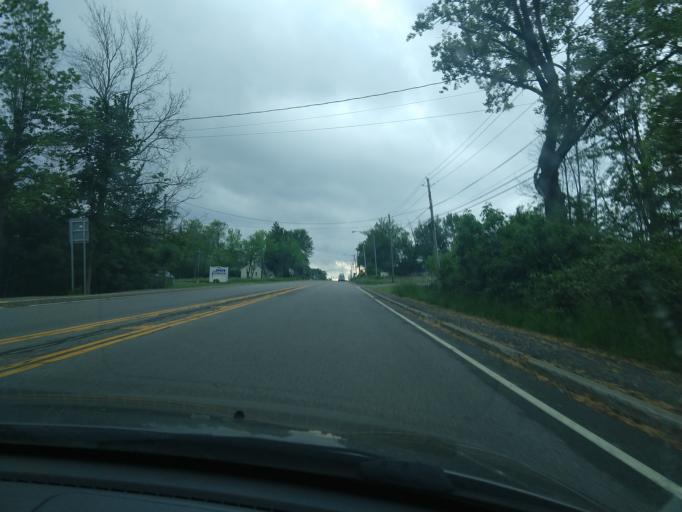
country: US
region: New York
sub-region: Erie County
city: Blasdell
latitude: 42.7674
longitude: -78.8242
